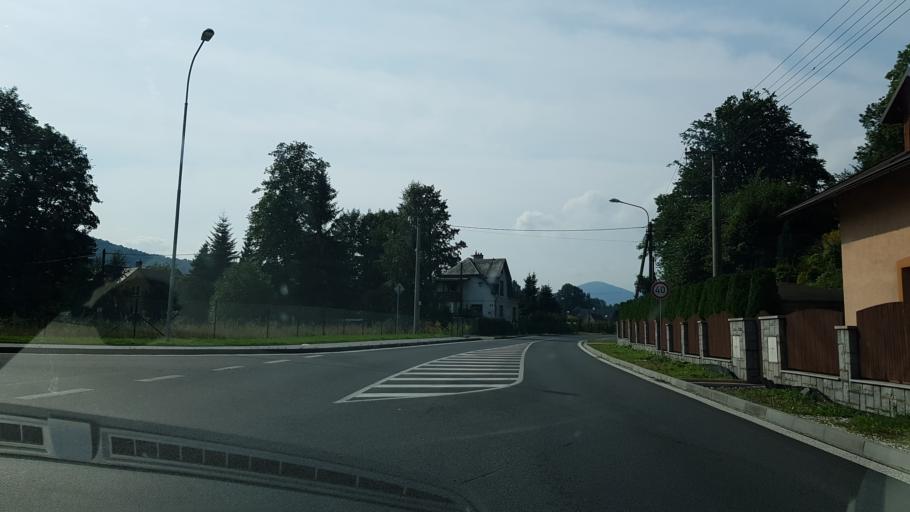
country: CZ
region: Olomoucky
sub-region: Okres Jesenik
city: Jesenik
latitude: 50.2197
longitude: 17.2082
